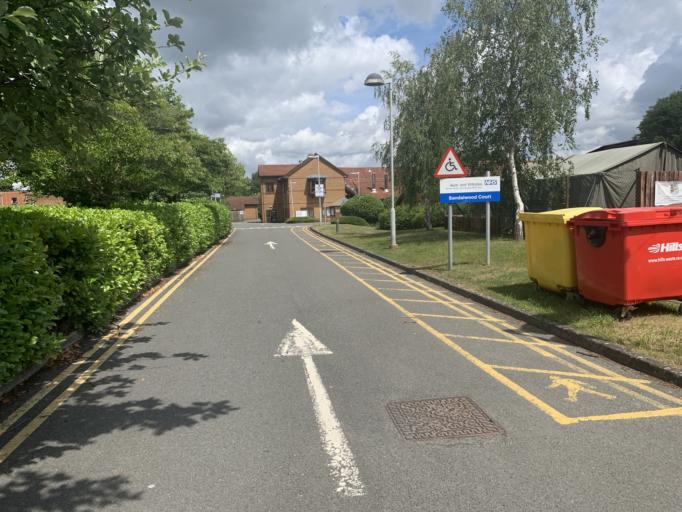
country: GB
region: England
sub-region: Borough of Swindon
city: Broad Blunsdon
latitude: 51.5874
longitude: -1.7484
